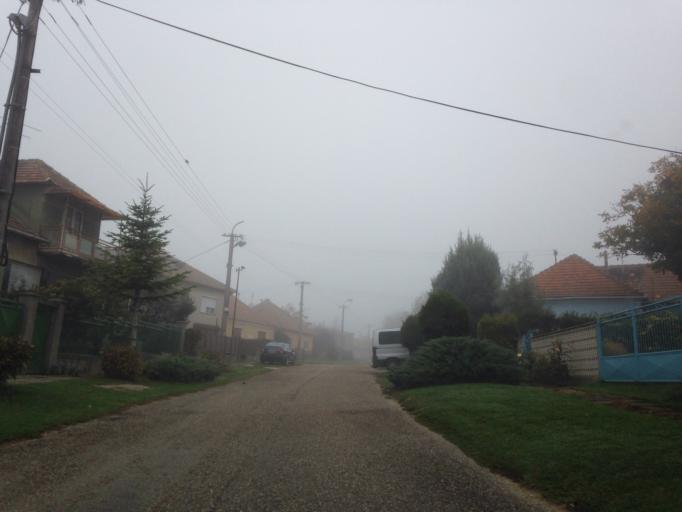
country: SK
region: Nitriansky
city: Svodin
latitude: 47.9064
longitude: 18.4144
